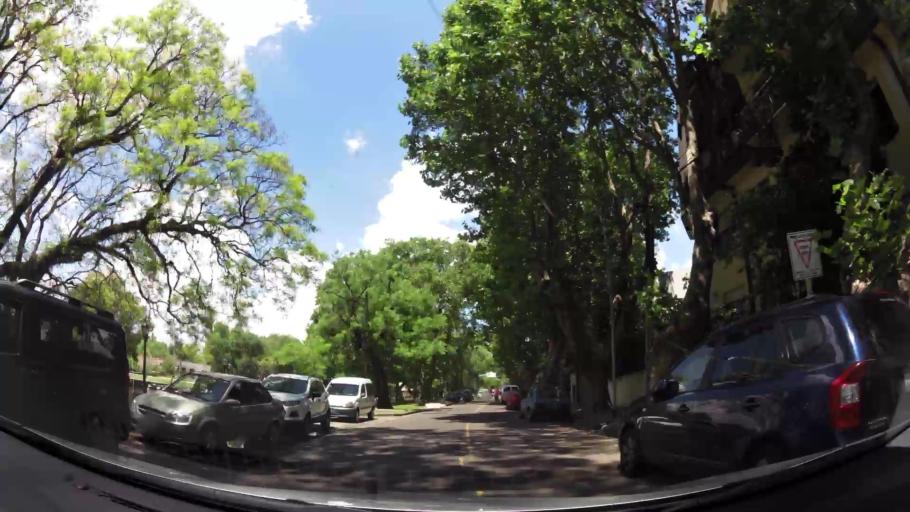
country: AR
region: Buenos Aires
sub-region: Partido de Tigre
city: Tigre
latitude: -34.4243
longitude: -58.5848
